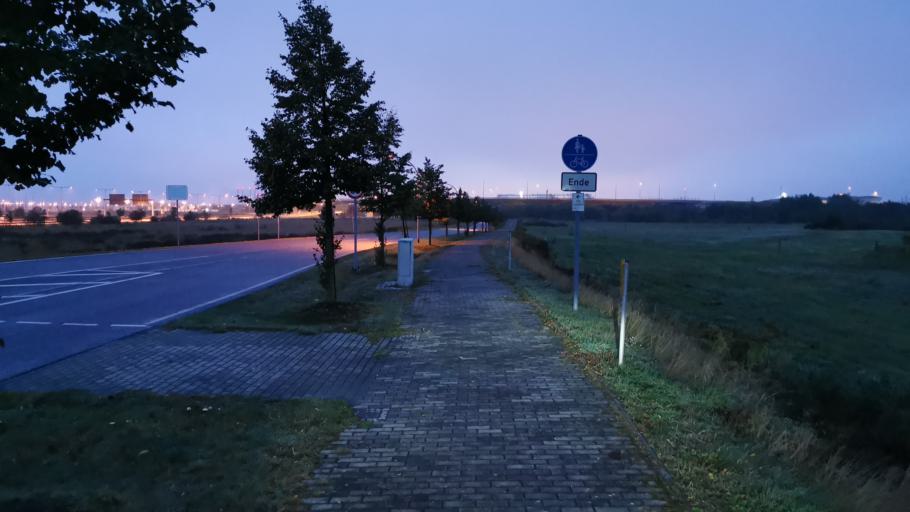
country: DE
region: Brandenburg
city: Schonefeld
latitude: 52.3722
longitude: 13.5388
